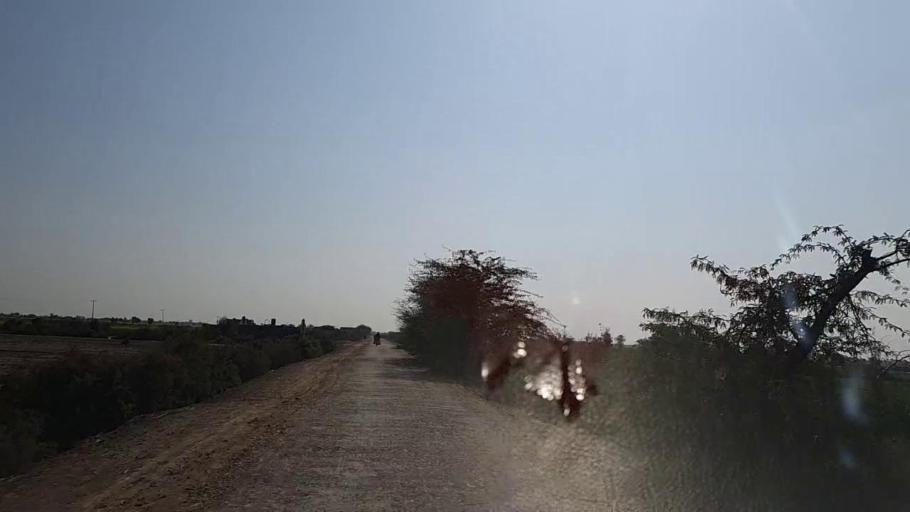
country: PK
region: Sindh
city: Sanghar
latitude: 25.9930
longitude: 69.0605
